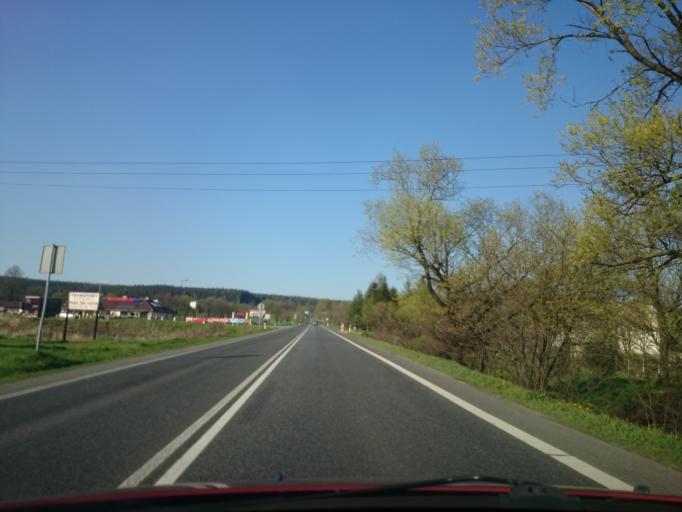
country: PL
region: Lower Silesian Voivodeship
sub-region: Powiat klodzki
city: Szczytna
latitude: 50.4161
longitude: 16.4500
